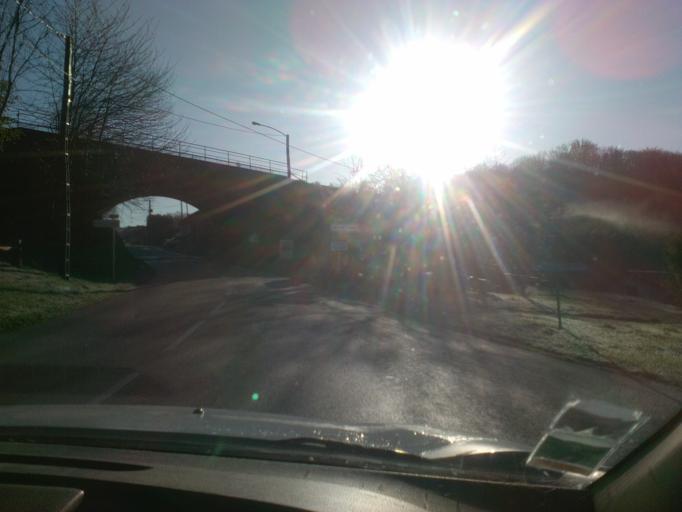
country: FR
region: Lorraine
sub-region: Departement des Vosges
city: Xertigny
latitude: 48.0516
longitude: 6.3763
